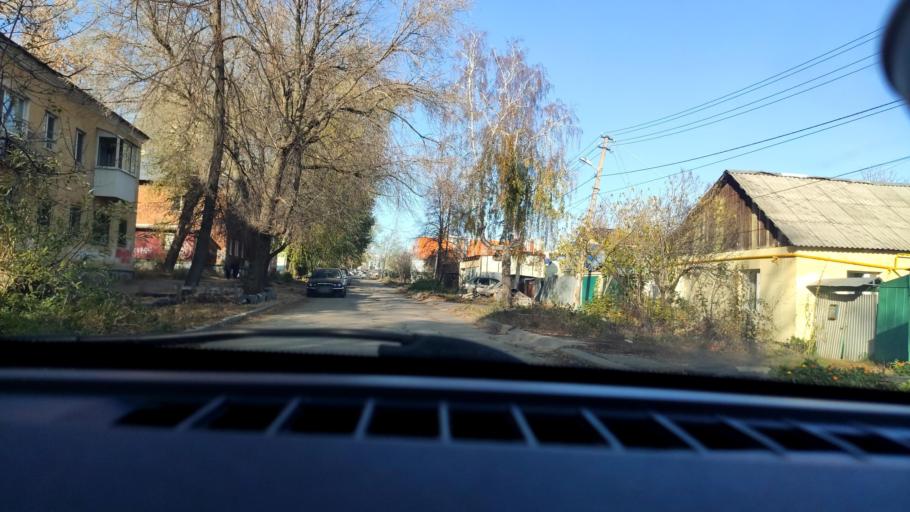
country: RU
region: Samara
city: Samara
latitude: 53.2025
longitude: 50.1941
